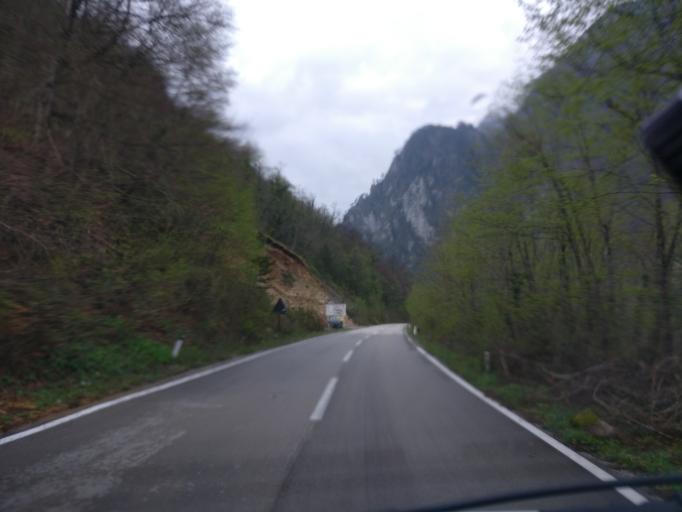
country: ME
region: Opstina Pluzine
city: Pluzine
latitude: 43.3096
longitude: 18.8526
